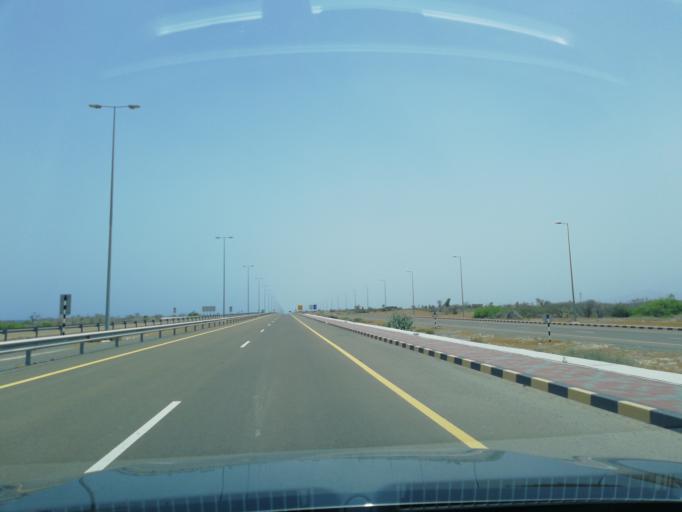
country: OM
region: Al Batinah
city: Shinas
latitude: 24.9161
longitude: 56.3893
